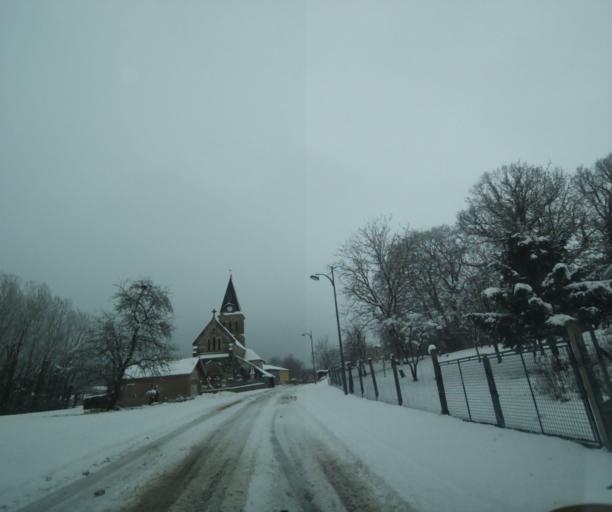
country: FR
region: Champagne-Ardenne
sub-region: Departement de la Haute-Marne
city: Montier-en-Der
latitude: 48.5356
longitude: 4.8140
